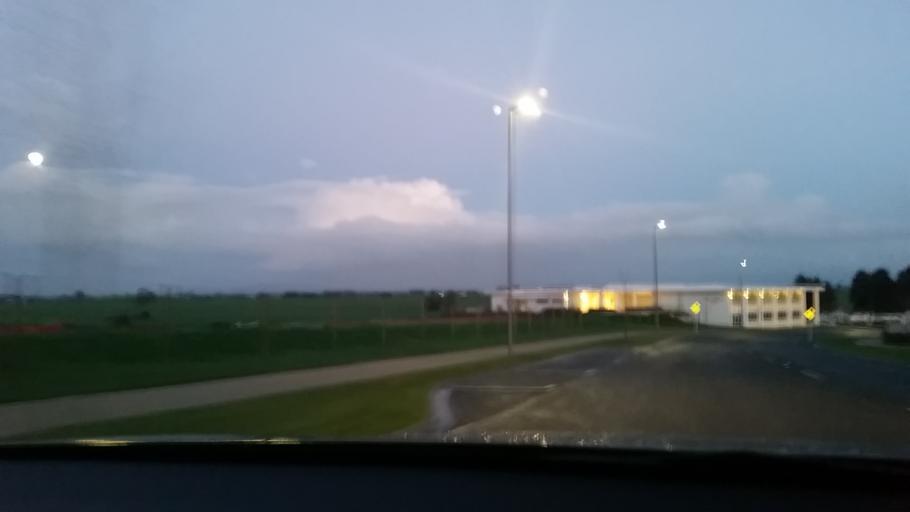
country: NZ
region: Waikato
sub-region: Hamilton City
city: Hamilton
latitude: -37.8196
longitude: 175.2264
